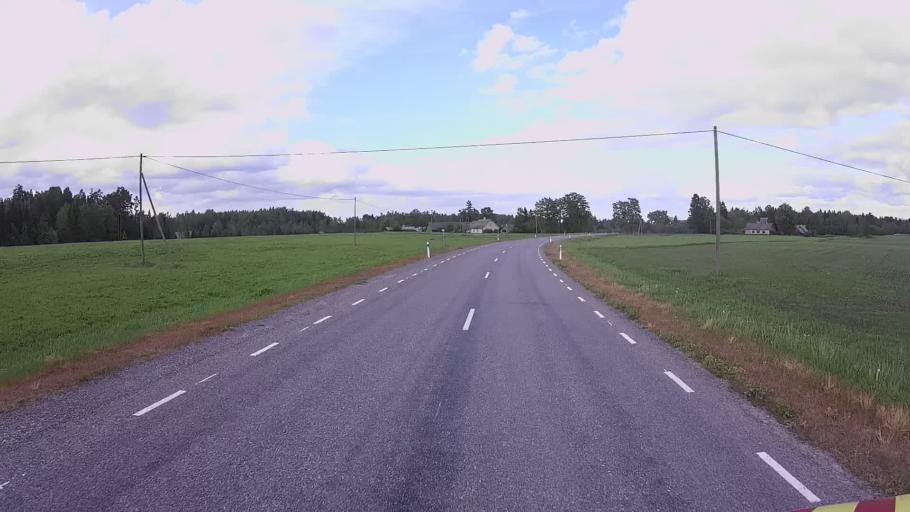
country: EE
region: Jogevamaa
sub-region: Mustvee linn
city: Mustvee
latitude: 59.0066
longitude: 26.9171
